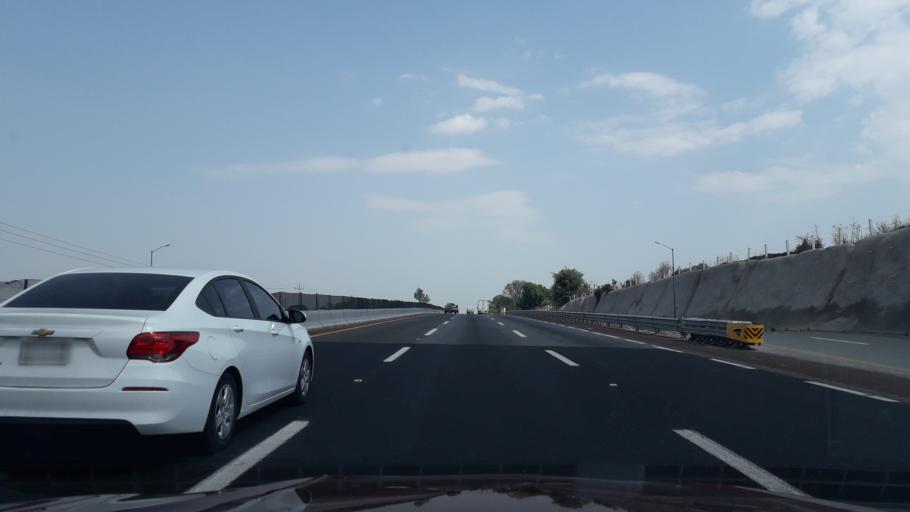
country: MX
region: Puebla
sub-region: San Salvador el Verde
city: San Lucas el Grande
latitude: 19.3086
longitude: -98.4952
